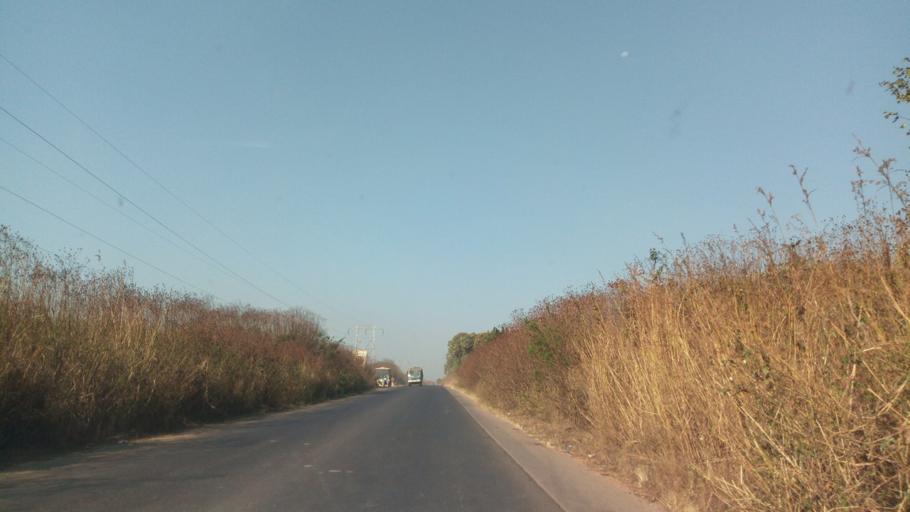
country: CD
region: Katanga
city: Likasi
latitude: -11.0028
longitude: 26.8496
